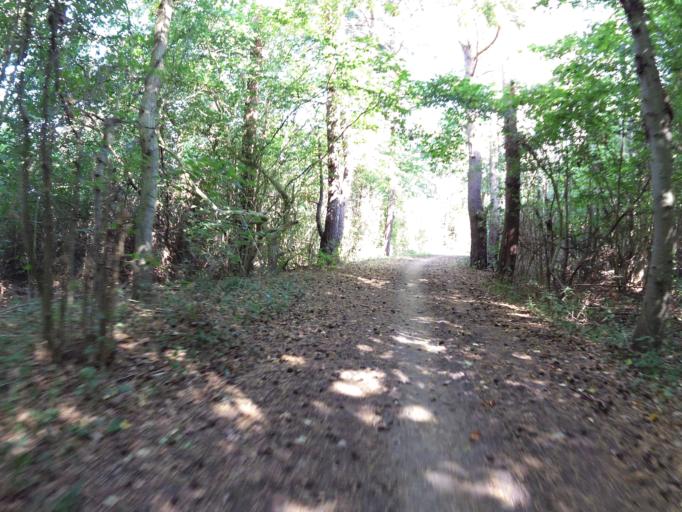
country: DE
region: Mecklenburg-Vorpommern
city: Loddin
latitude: 53.9613
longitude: 14.0433
